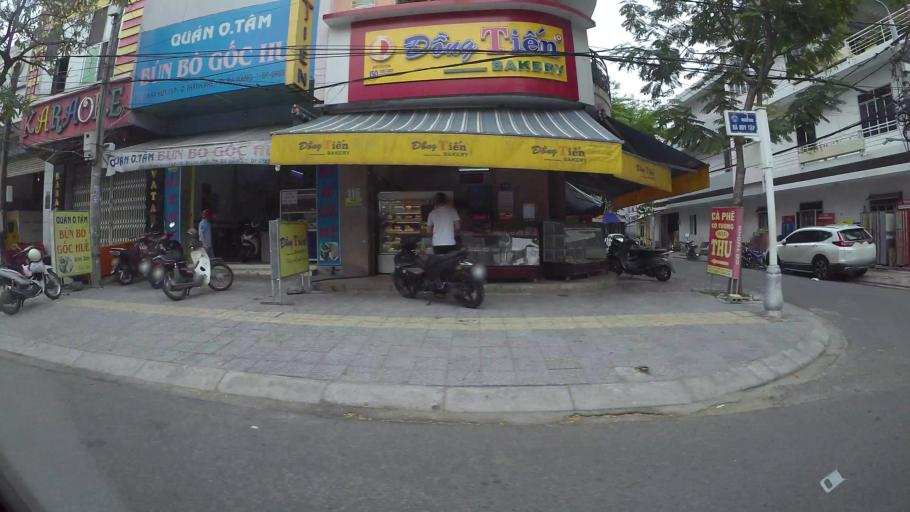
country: VN
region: Da Nang
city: Thanh Khe
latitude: 16.0669
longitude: 108.1919
